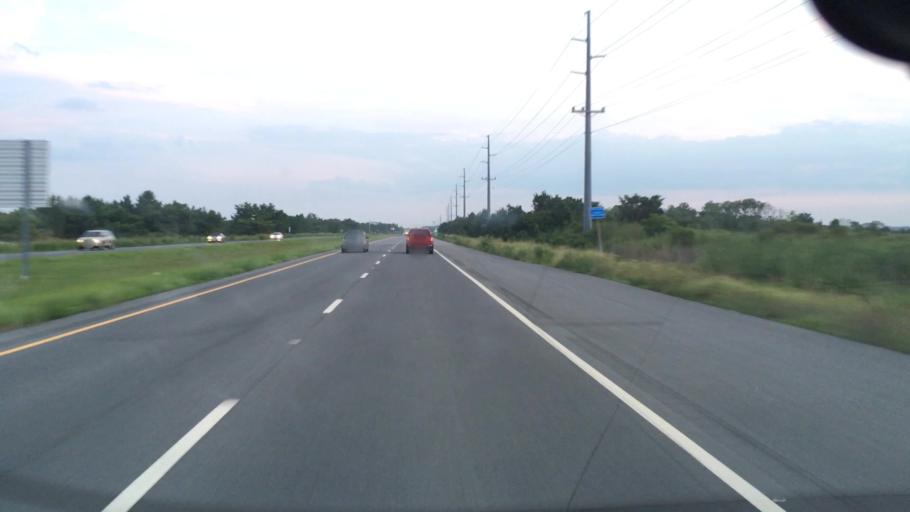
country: US
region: Delaware
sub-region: Sussex County
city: Bethany Beach
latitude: 38.5979
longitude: -75.0625
